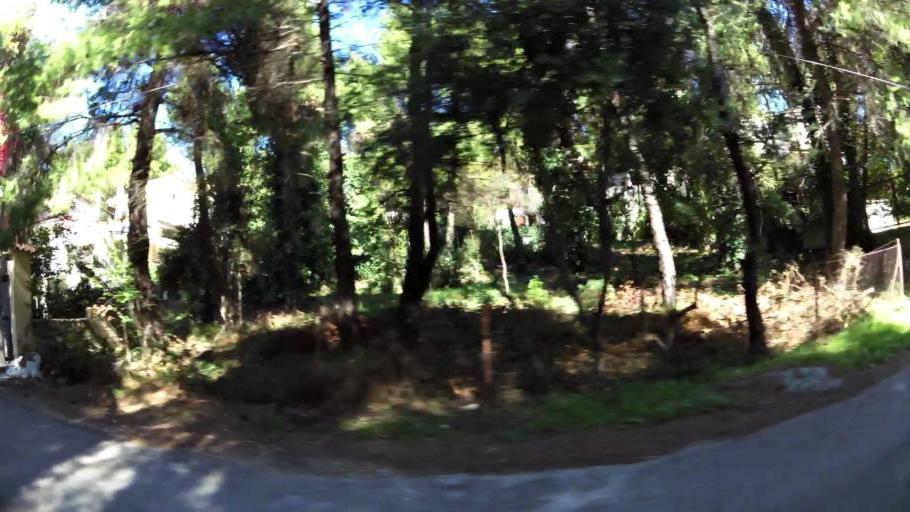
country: GR
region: Attica
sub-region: Nomarchia Anatolikis Attikis
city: Dionysos
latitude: 38.1030
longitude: 23.8884
